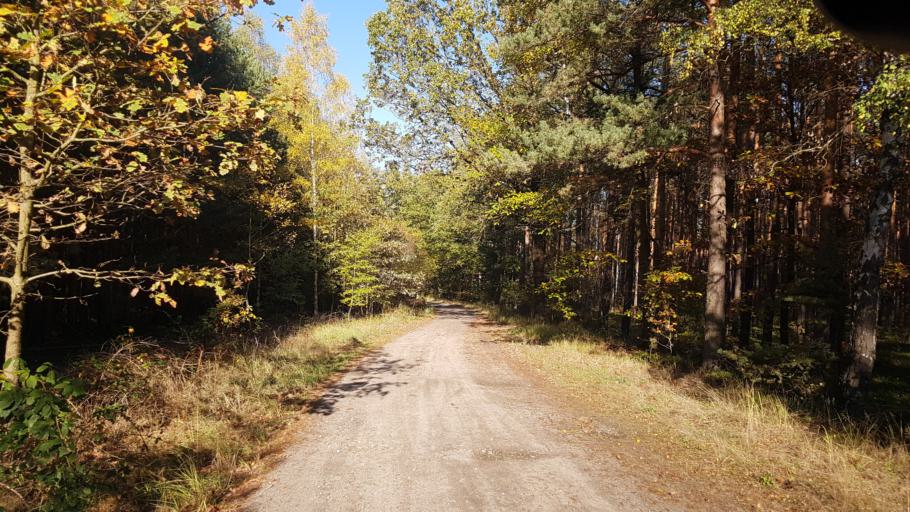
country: DE
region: Brandenburg
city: Ruckersdorf
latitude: 51.5486
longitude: 13.5364
